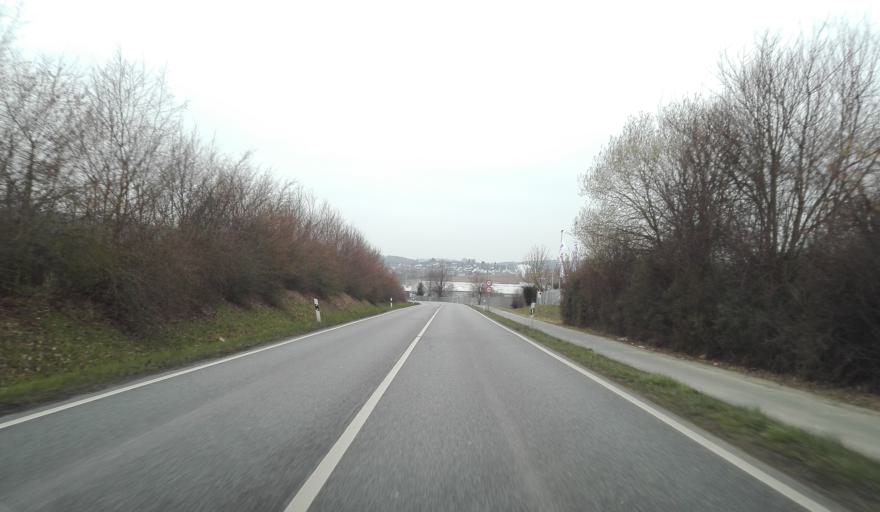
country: DE
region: Hesse
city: Ober-Ramstadt
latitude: 49.8191
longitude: 8.7615
